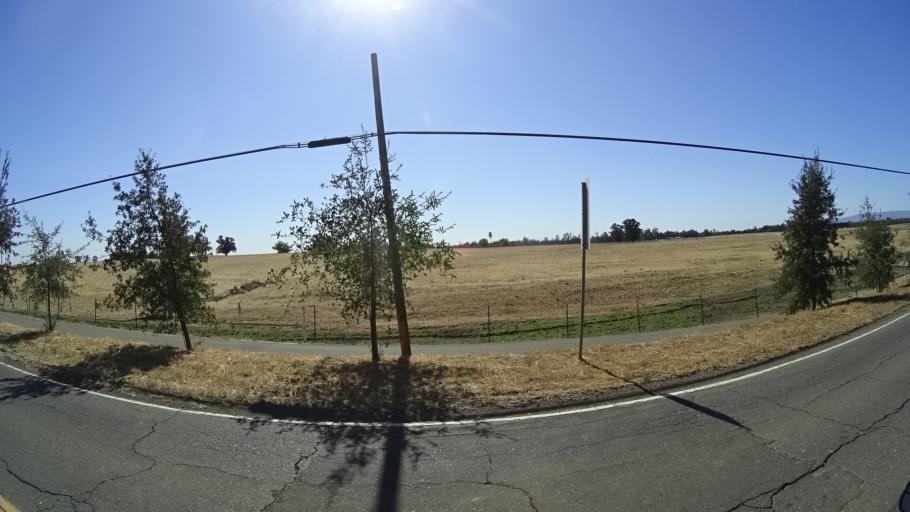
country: US
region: California
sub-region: Yolo County
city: Davis
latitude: 38.5470
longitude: -121.8423
